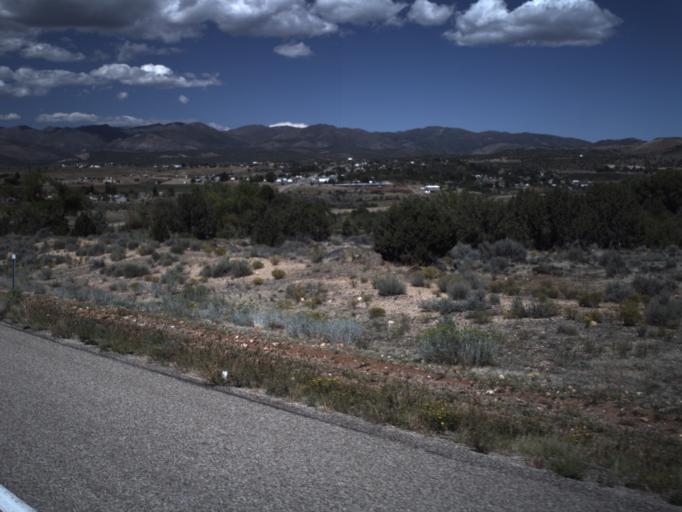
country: US
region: Utah
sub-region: Washington County
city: Ivins
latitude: 37.3222
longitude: -113.6913
